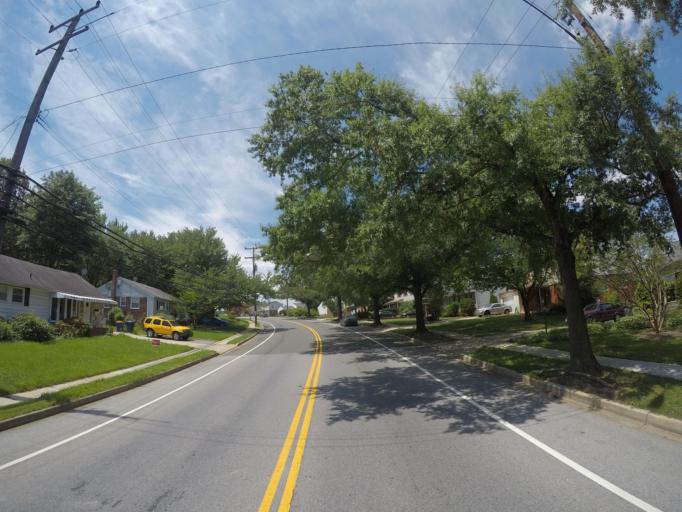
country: US
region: Maryland
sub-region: Prince George's County
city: New Carrollton
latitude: 38.9767
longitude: -76.8792
